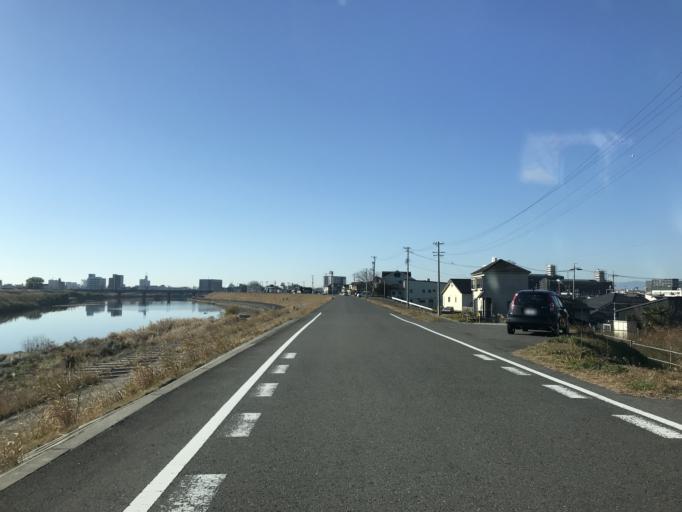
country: JP
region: Aichi
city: Nagoya-shi
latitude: 35.2003
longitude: 136.8731
